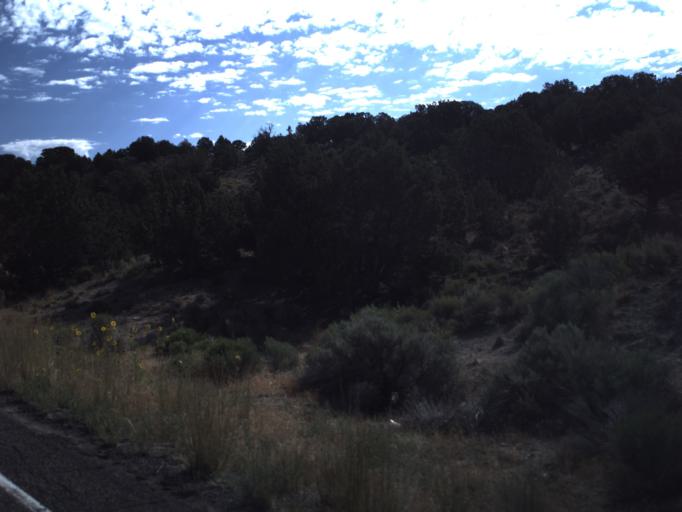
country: US
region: Utah
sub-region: Juab County
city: Mona
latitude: 39.7592
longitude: -112.1786
